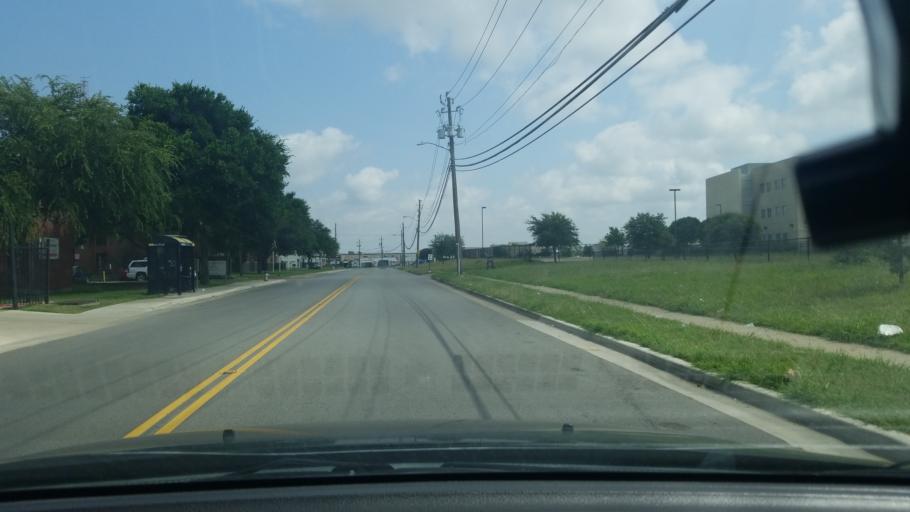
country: US
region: Texas
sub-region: Dallas County
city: Mesquite
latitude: 32.8008
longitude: -96.6882
